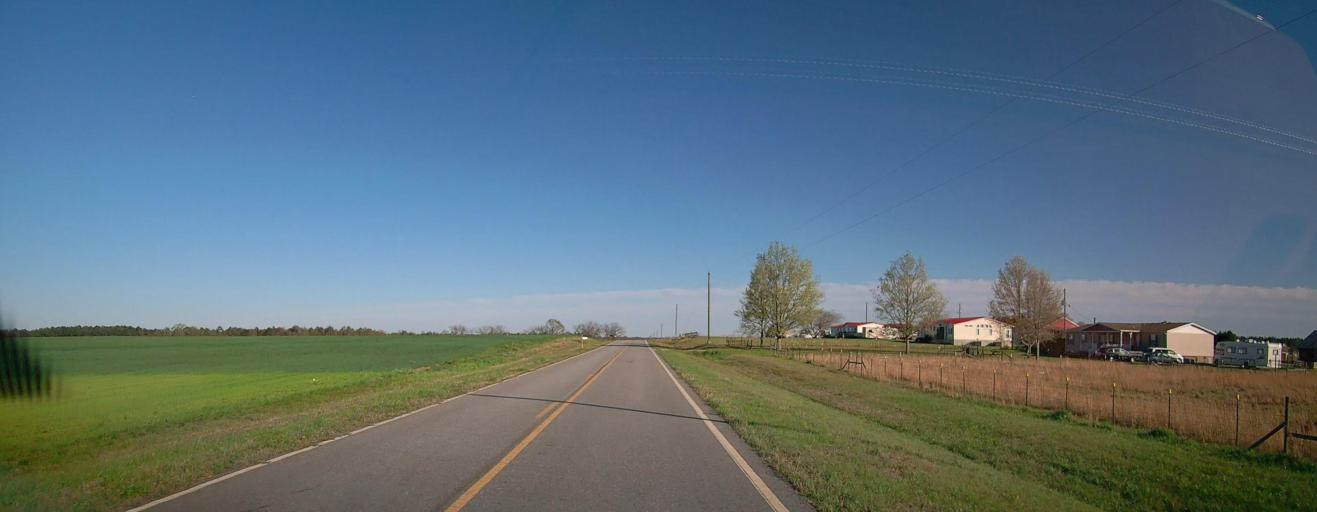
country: US
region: Georgia
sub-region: Dooly County
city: Unadilla
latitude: 32.3567
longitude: -83.6388
